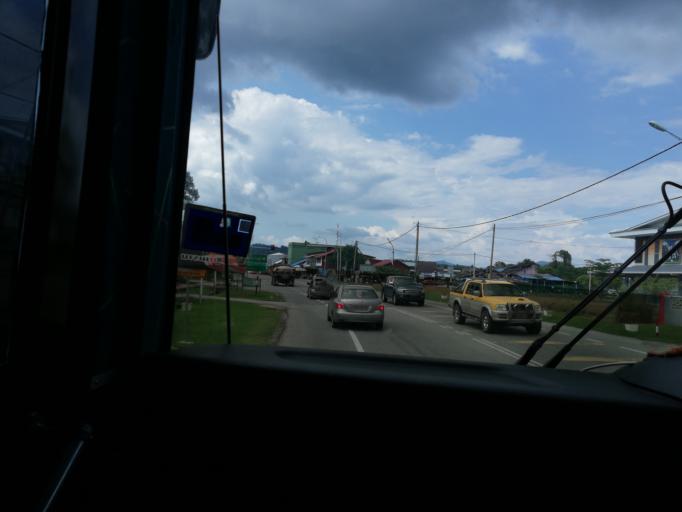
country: MY
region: Penang
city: Nibong Tebal
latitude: 5.2069
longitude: 100.6127
